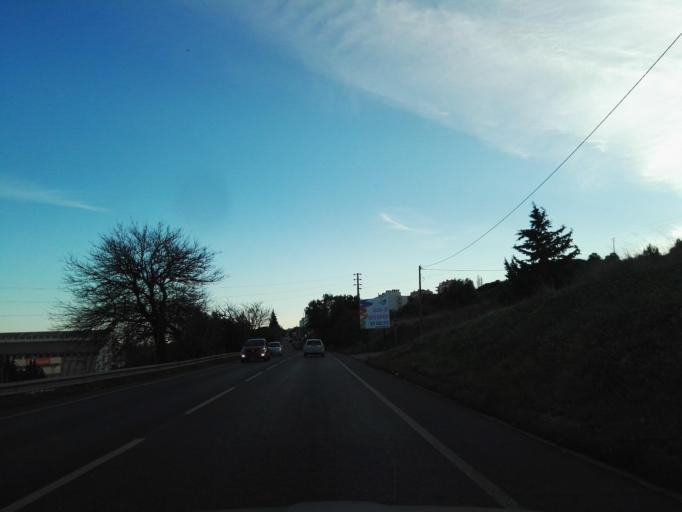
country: PT
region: Lisbon
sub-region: Vila Franca de Xira
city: Vialonga
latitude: 38.8819
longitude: -9.0503
